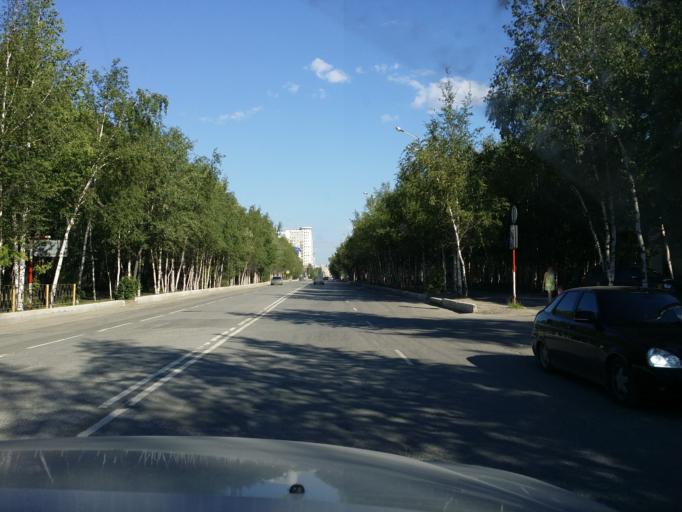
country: RU
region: Khanty-Mansiyskiy Avtonomnyy Okrug
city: Nizhnevartovsk
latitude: 60.9377
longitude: 76.5676
